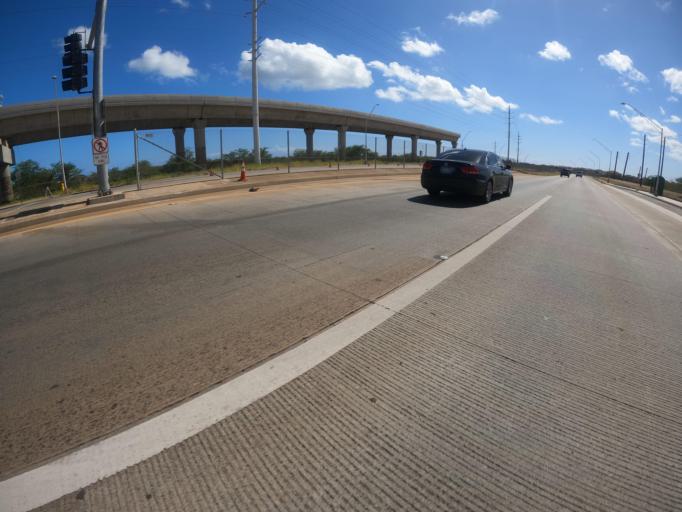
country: US
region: Hawaii
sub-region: Honolulu County
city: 'Ewa Villages
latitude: 21.3454
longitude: -158.0519
